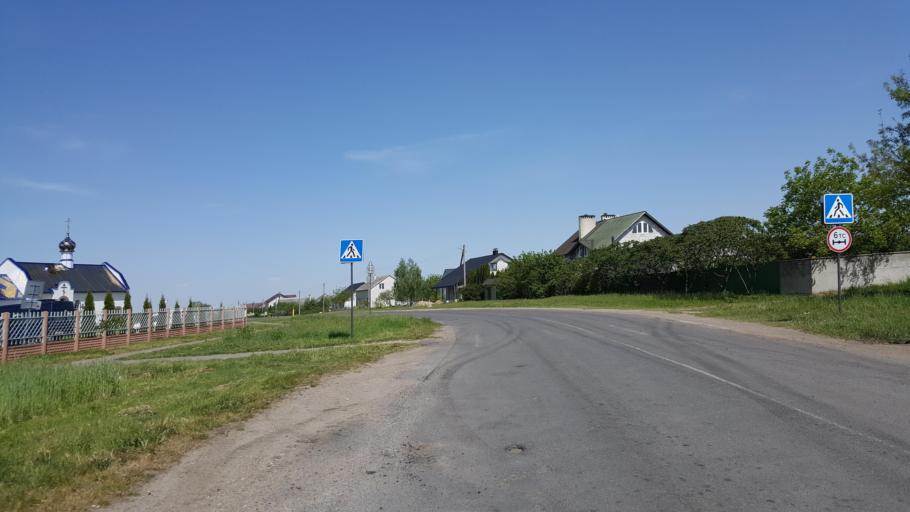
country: BY
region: Brest
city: Brest
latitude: 52.1614
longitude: 23.6659
